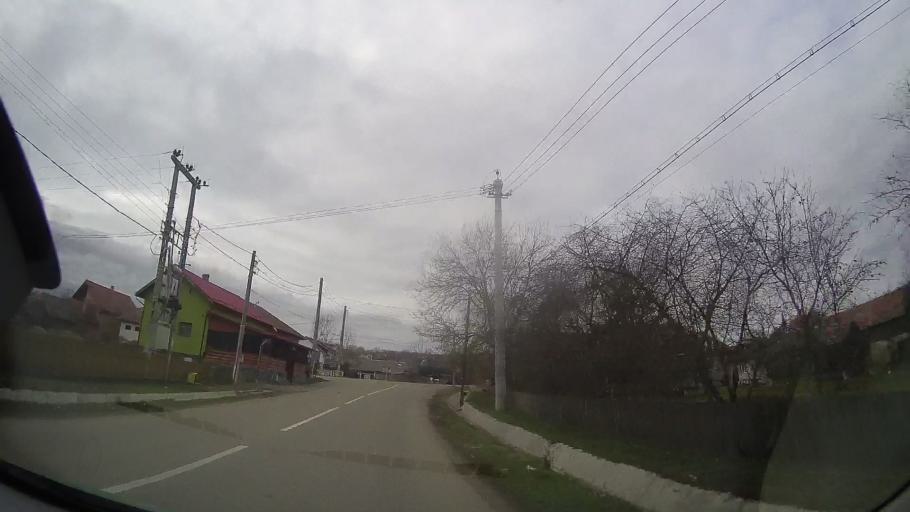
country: RO
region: Bistrita-Nasaud
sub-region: Comuna Milas
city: Milas
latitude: 46.8202
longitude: 24.4374
